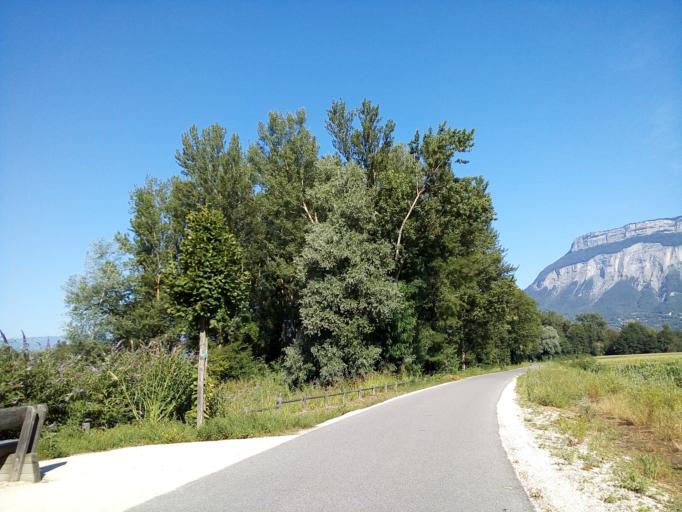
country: FR
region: Rhone-Alpes
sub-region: Departement de l'Isere
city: Domene
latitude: 45.2037
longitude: 5.8191
